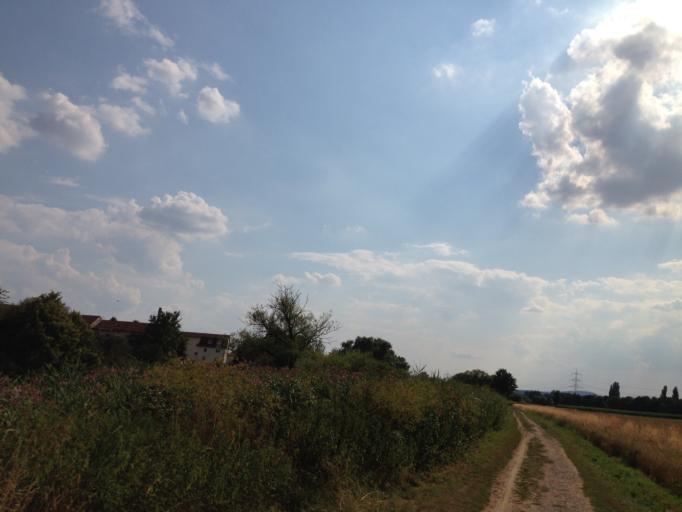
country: DE
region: Hesse
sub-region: Regierungsbezirk Giessen
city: Heuchelheim
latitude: 50.5780
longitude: 8.6548
